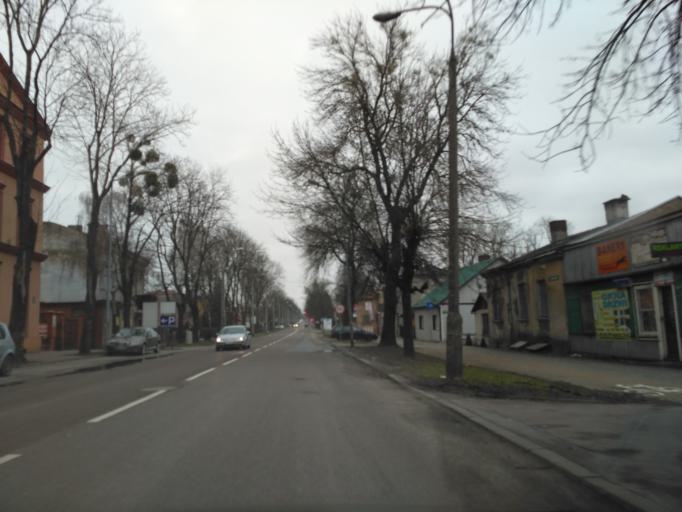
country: PL
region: Lublin Voivodeship
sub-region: Chelm
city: Chelm
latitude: 51.1283
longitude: 23.4861
